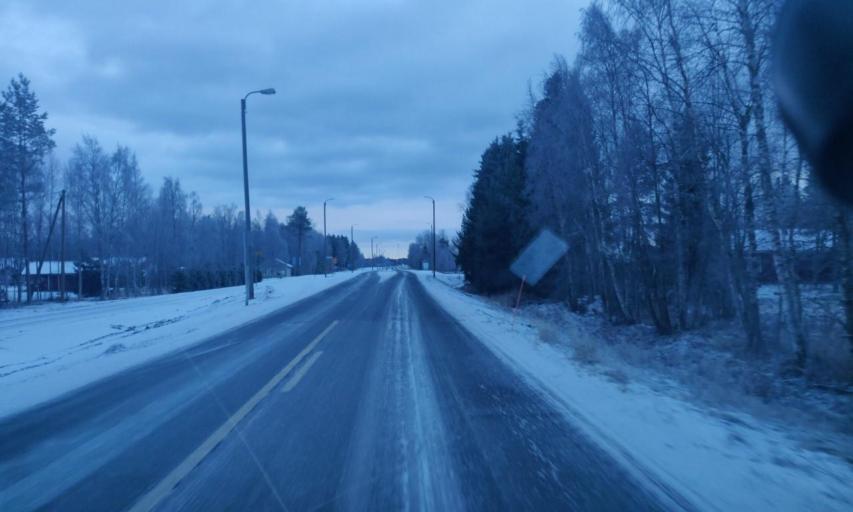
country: FI
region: Northern Ostrobothnia
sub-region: Oulu
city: Oulunsalo
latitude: 64.9863
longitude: 25.2618
